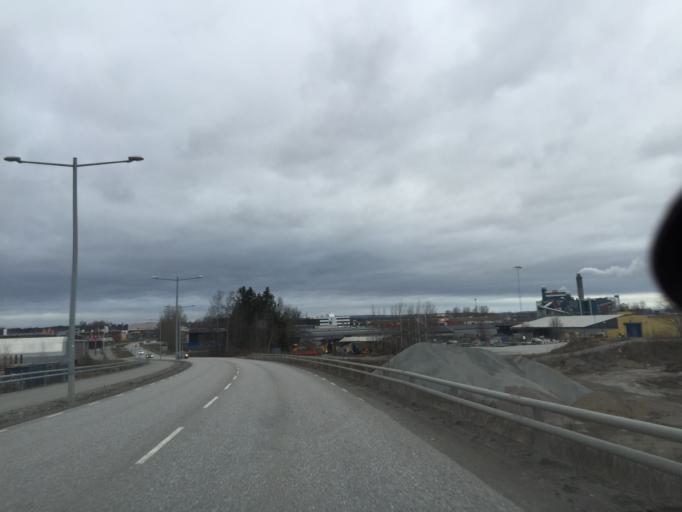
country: SE
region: OErebro
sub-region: Orebro Kommun
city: Orebro
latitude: 59.2559
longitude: 15.1836
